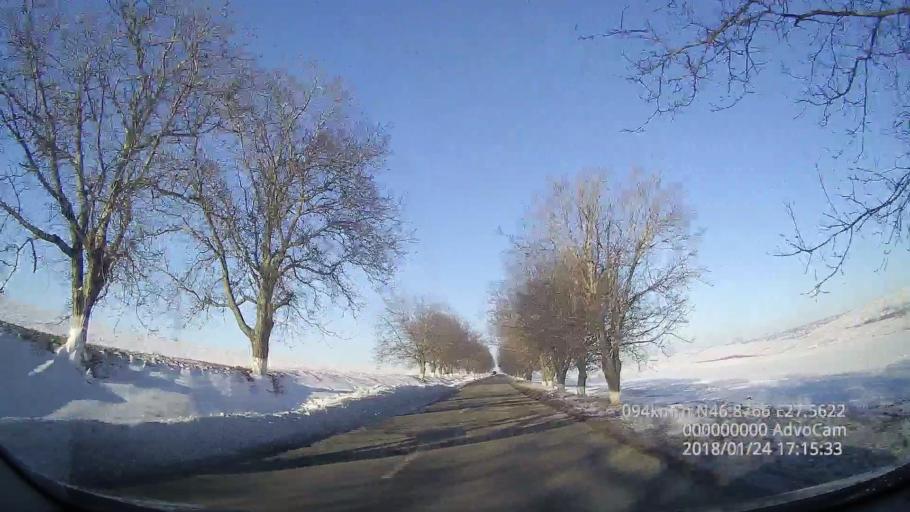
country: RO
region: Vaslui
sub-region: Comuna Rebricea
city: Rebricea
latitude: 46.8774
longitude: 27.5624
